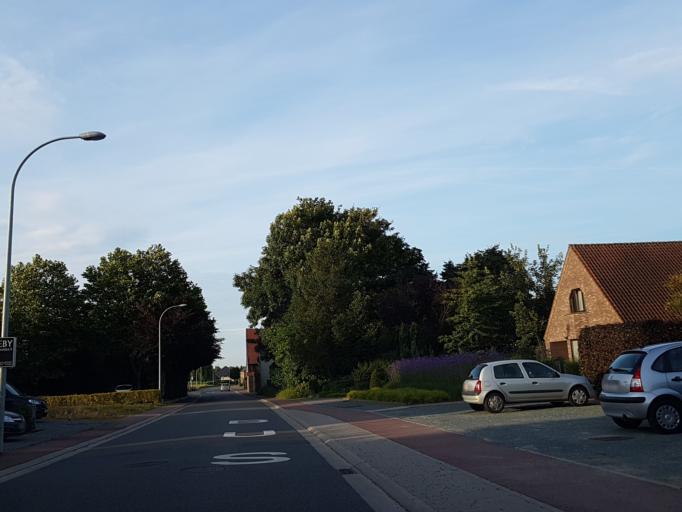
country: BE
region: Flanders
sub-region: Provincie Vlaams-Brabant
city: Merchtem
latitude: 50.9815
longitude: 4.2537
